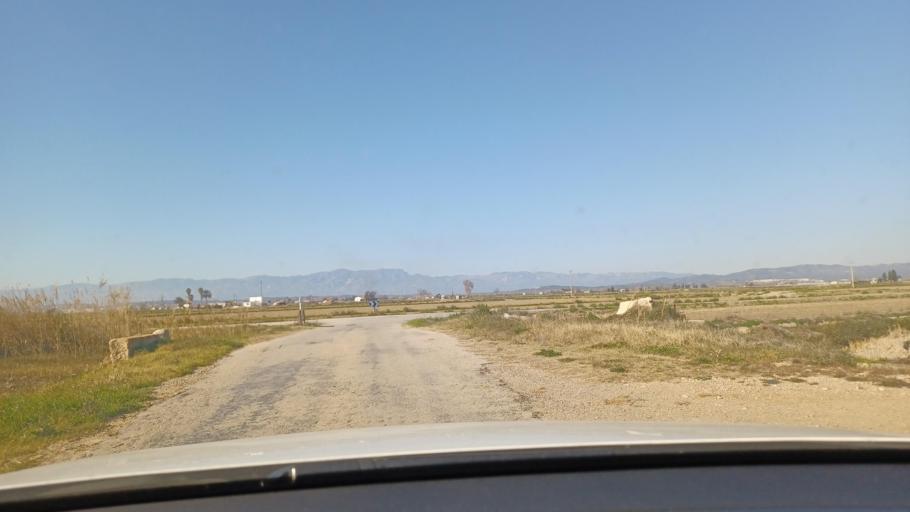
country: ES
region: Catalonia
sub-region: Provincia de Tarragona
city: Amposta
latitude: 40.6987
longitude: 0.6451
